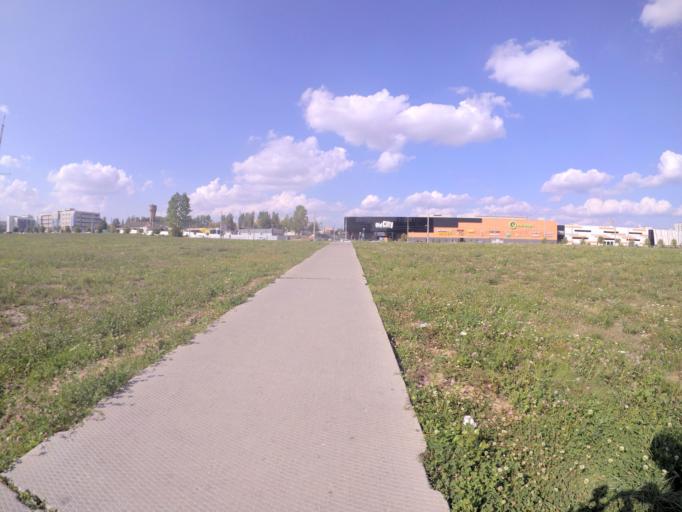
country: BY
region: Grodnenskaya
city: Hrodna
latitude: 53.6999
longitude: 23.8338
